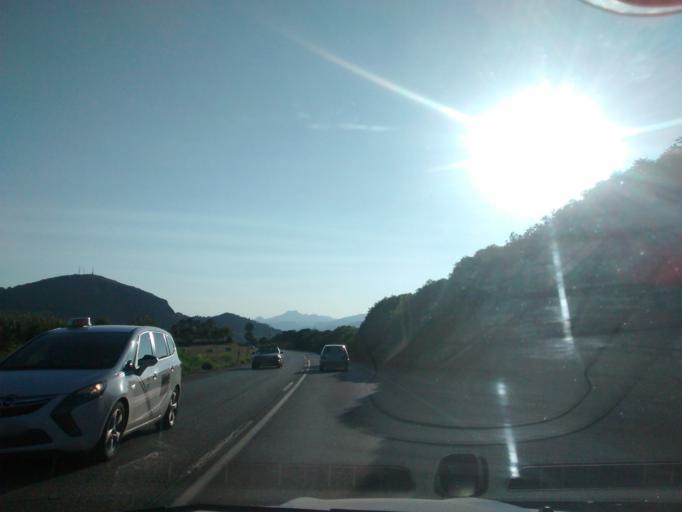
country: ES
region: Balearic Islands
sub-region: Illes Balears
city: Alcudia
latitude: 39.8458
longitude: 3.1212
